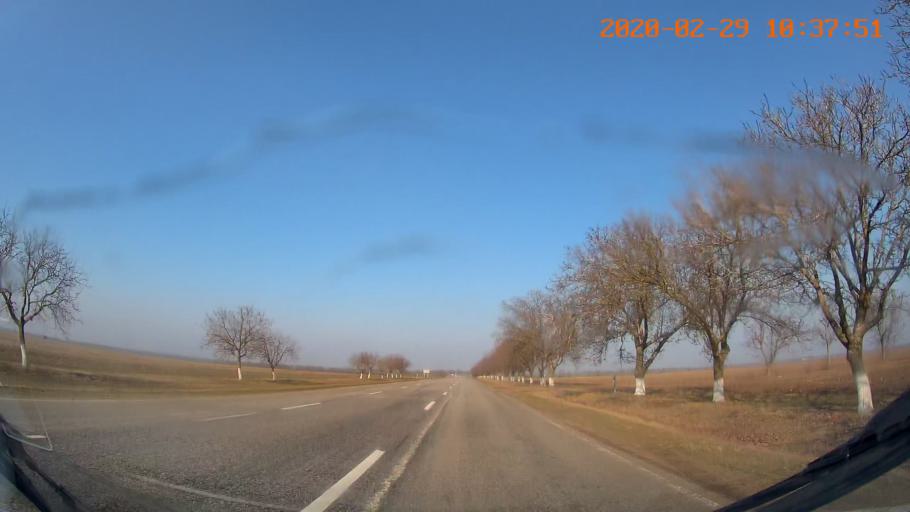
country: MD
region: Anenii Noi
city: Varnita
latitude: 47.0104
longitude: 29.4831
